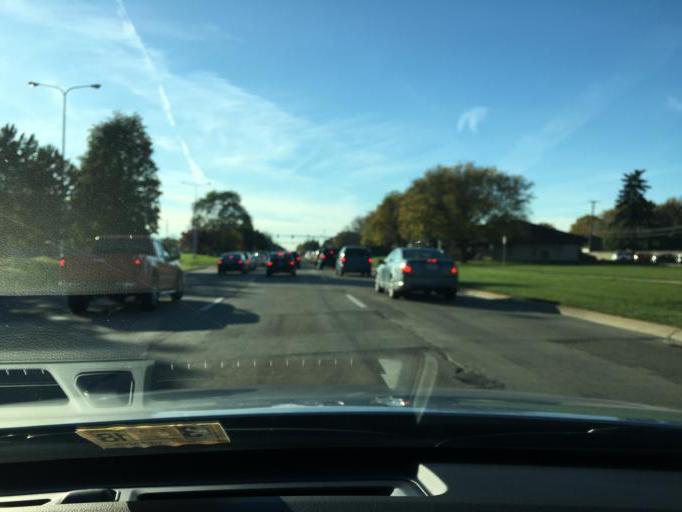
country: US
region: Michigan
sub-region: Macomb County
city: Sterling Heights
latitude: 42.5648
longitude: -83.0662
